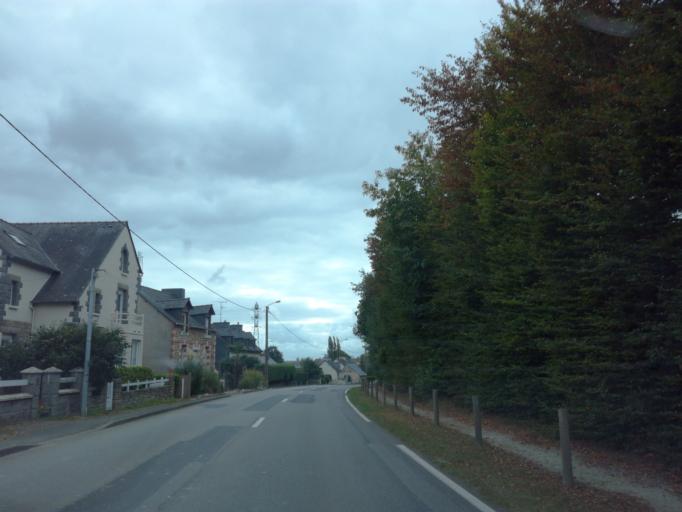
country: FR
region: Brittany
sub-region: Departement des Cotes-d'Armor
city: Loudeac
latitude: 48.1688
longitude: -2.7534
